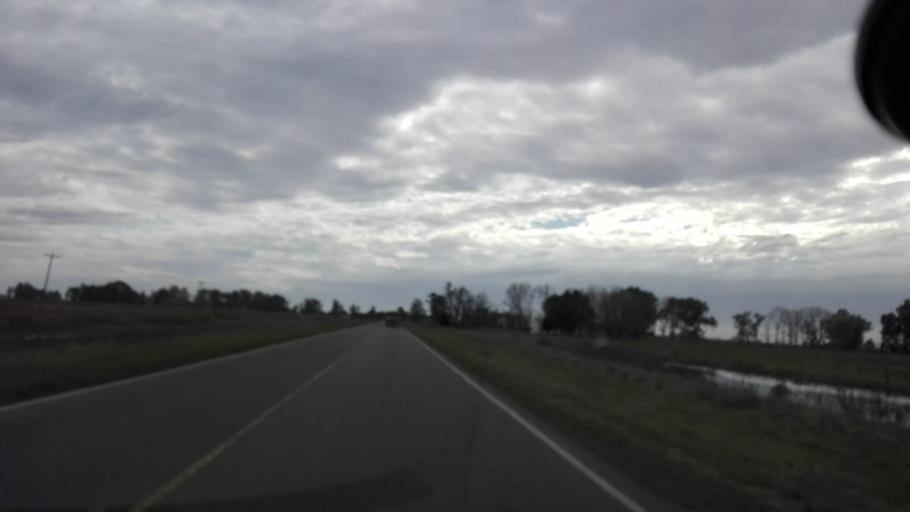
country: AR
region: Buenos Aires
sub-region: Partido de Las Flores
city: Las Flores
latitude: -36.2147
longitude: -59.0451
